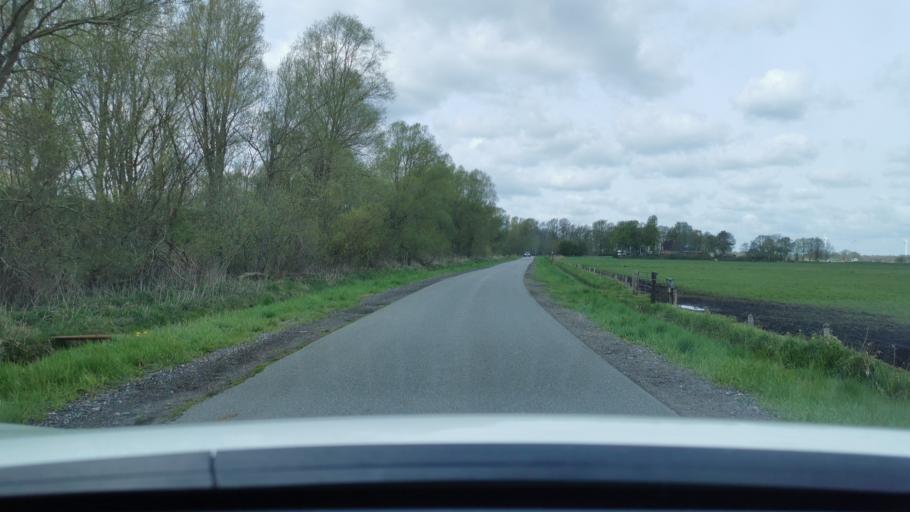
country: DE
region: Schleswig-Holstein
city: Oldenbuttel
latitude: 54.1819
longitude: 9.4475
